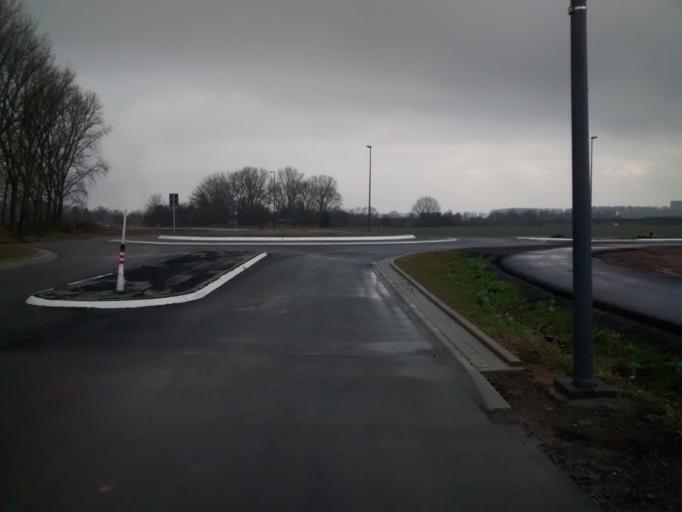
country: DE
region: North Rhine-Westphalia
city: Monheim am Rhein
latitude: 51.0408
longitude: 6.9084
